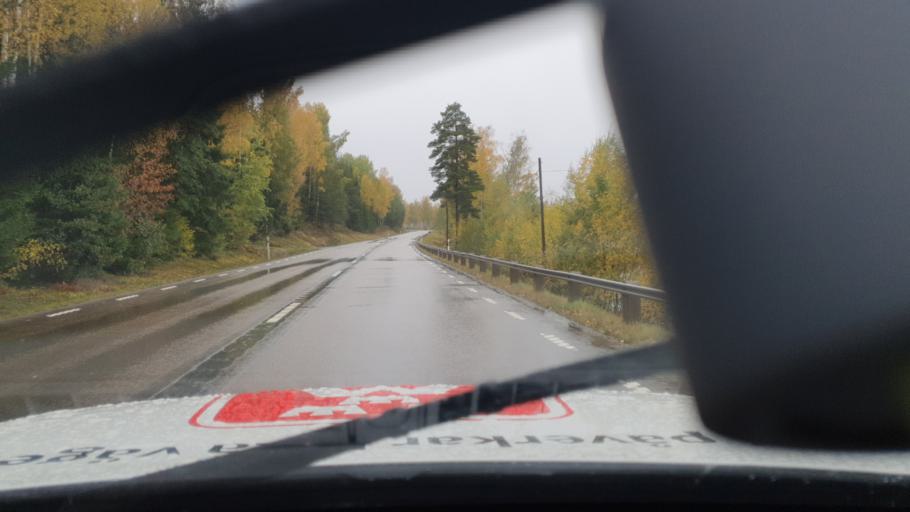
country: SE
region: Vaestra Goetaland
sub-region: Bengtsfors Kommun
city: Billingsfors
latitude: 58.9334
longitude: 12.1285
